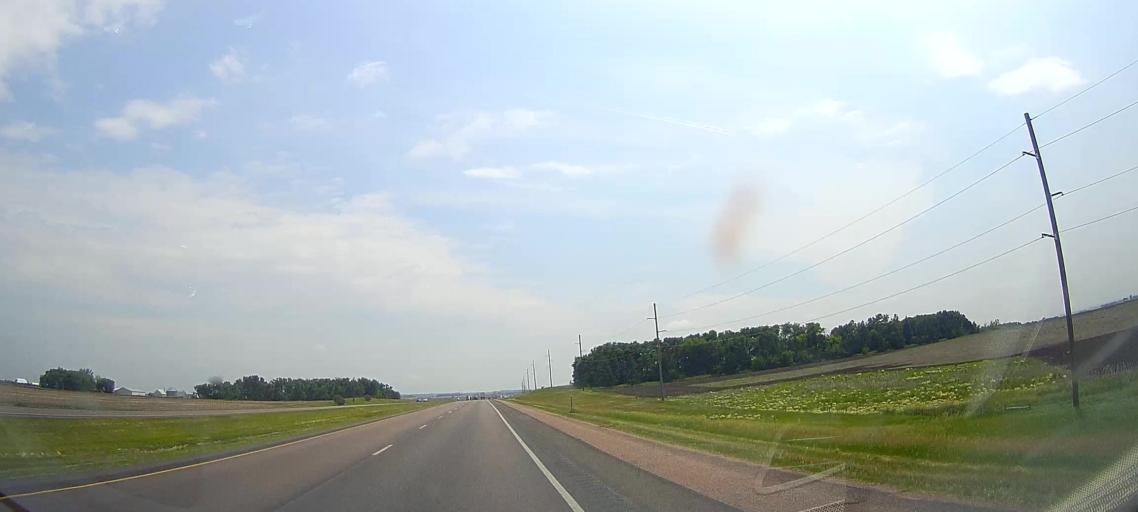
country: US
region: South Dakota
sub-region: Union County
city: Beresford
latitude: 43.1596
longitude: -96.7960
